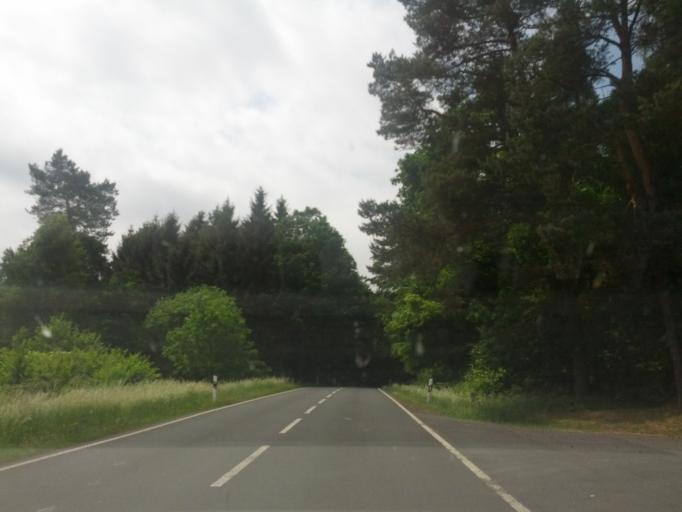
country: DE
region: Thuringia
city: Marksuhl
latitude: 50.8962
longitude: 10.1898
